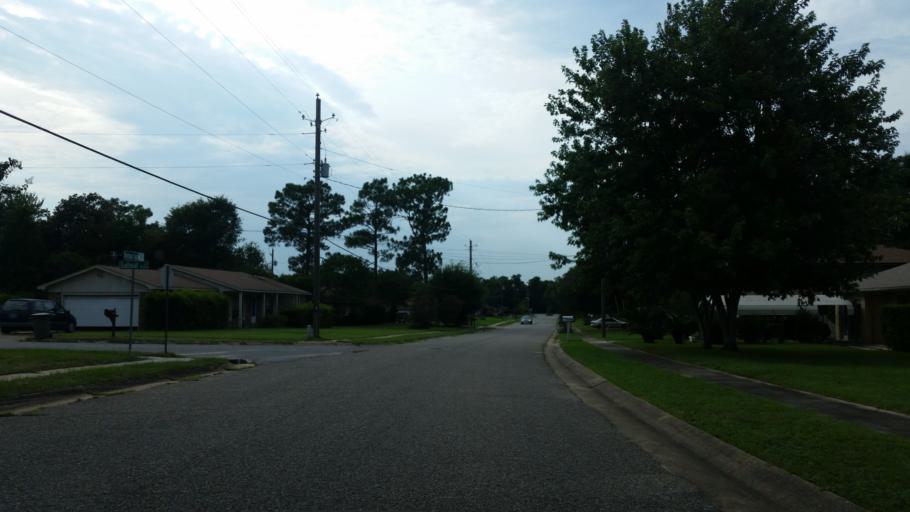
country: US
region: Florida
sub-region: Escambia County
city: Ferry Pass
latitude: 30.5136
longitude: -87.1755
